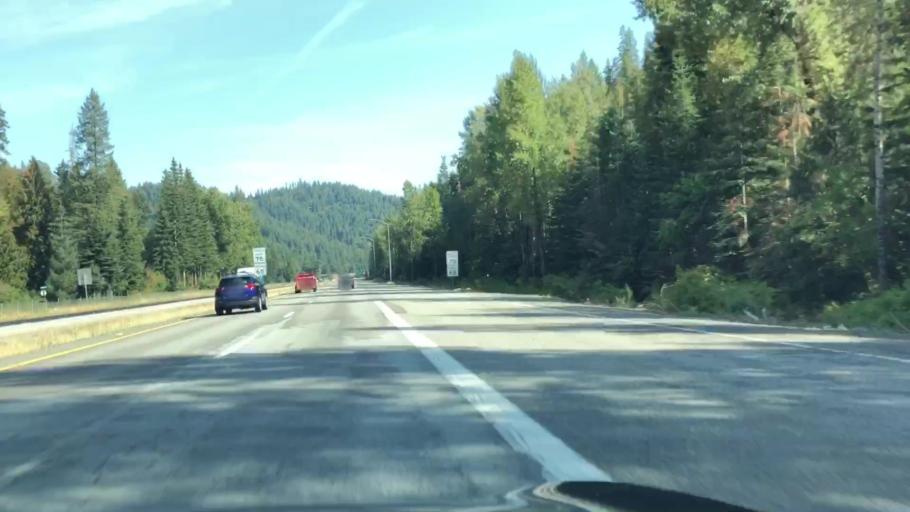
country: US
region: Idaho
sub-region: Shoshone County
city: Pinehurst
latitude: 47.5785
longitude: -116.4560
